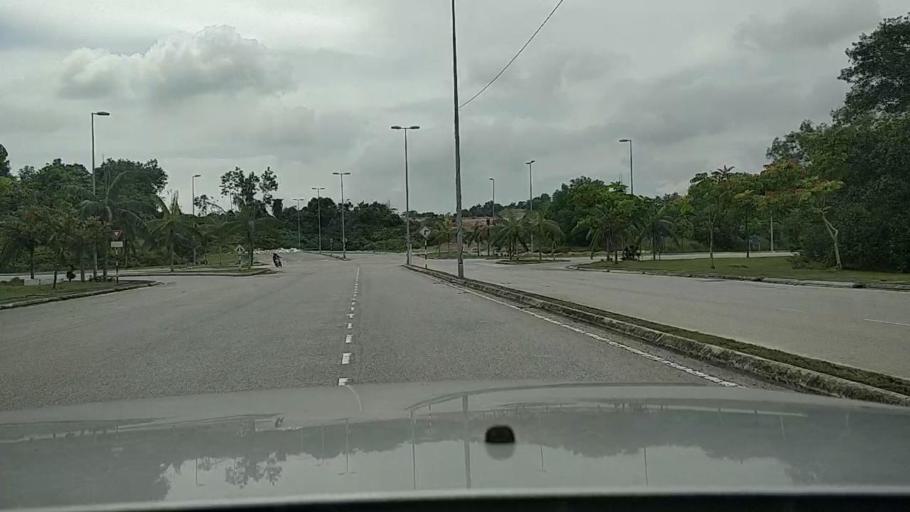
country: MY
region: Putrajaya
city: Putrajaya
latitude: 2.8980
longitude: 101.6456
